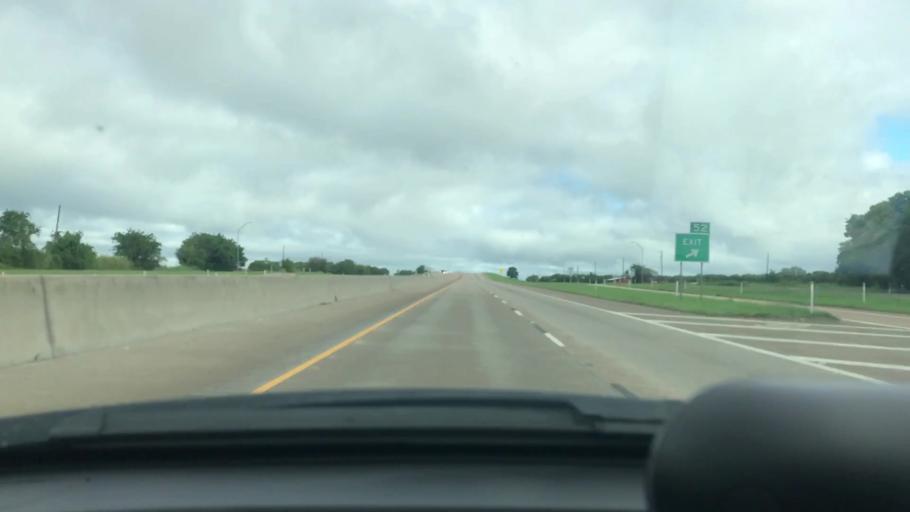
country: US
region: Texas
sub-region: Grayson County
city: Howe
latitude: 33.4601
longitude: -96.6099
